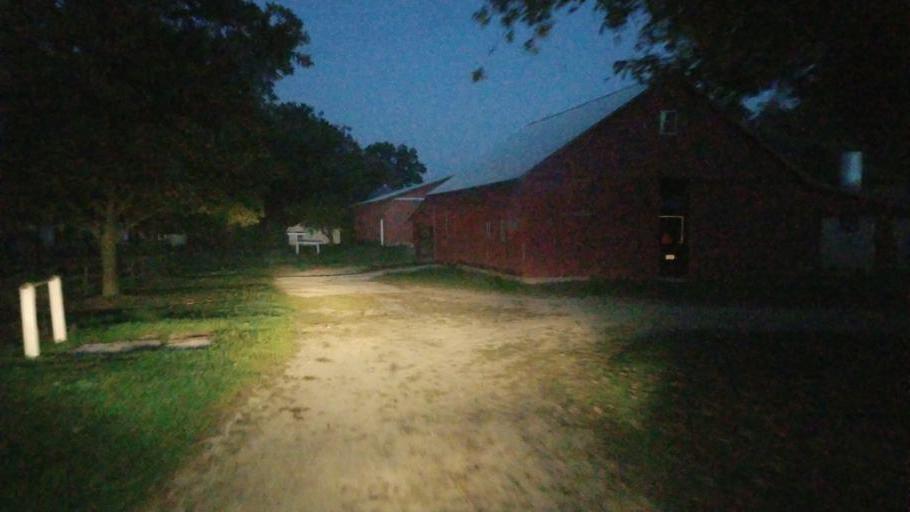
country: US
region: Indiana
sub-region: Elkhart County
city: Middlebury
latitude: 41.6907
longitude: -85.6685
